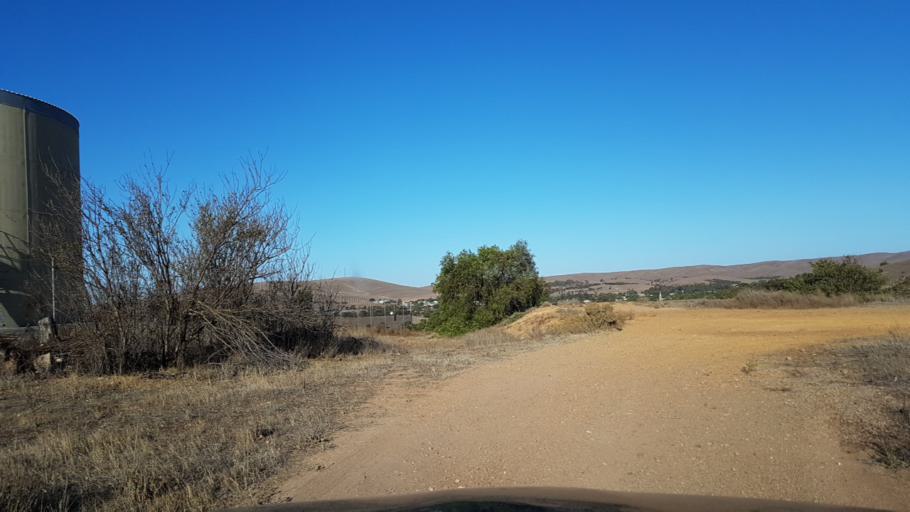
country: AU
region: South Australia
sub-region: Clare and Gilbert Valleys
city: Clare
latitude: -33.6755
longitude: 138.9273
